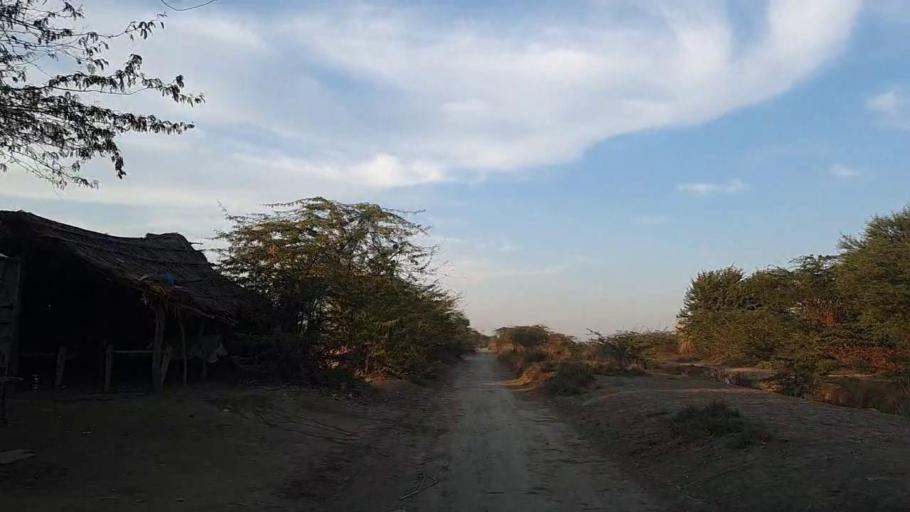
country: PK
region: Sindh
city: Bandhi
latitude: 26.6030
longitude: 68.3591
